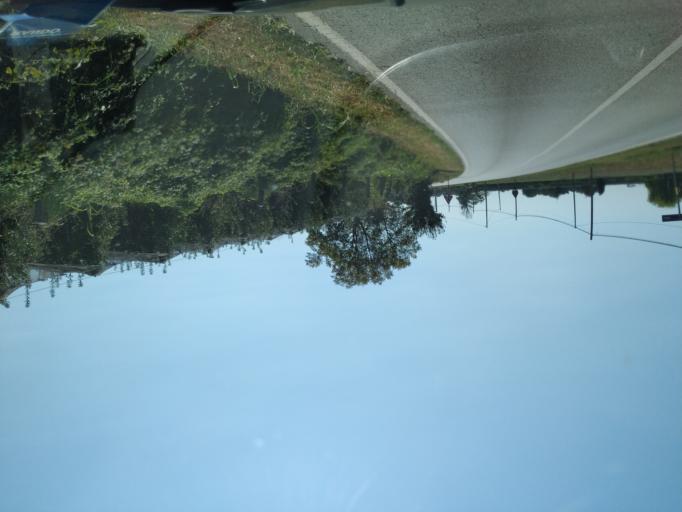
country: IT
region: Emilia-Romagna
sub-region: Provincia di Ferrara
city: Copparo
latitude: 44.8905
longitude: 11.8447
